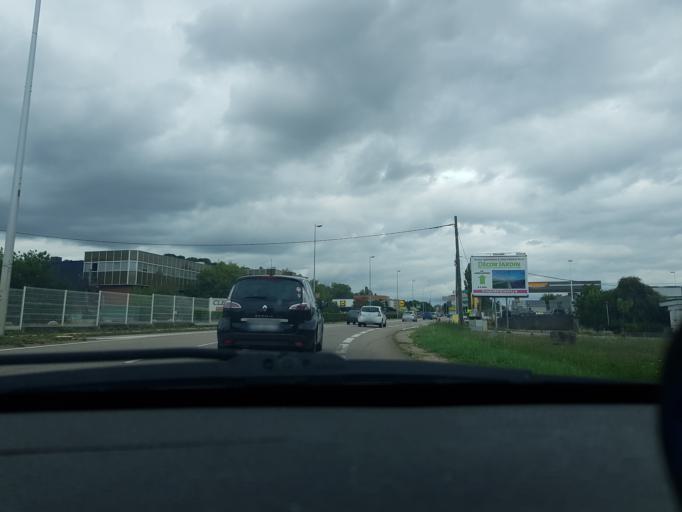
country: FR
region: Lorraine
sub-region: Departement de Meurthe-et-Moselle
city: Seichamps
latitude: 48.7126
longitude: 6.2485
